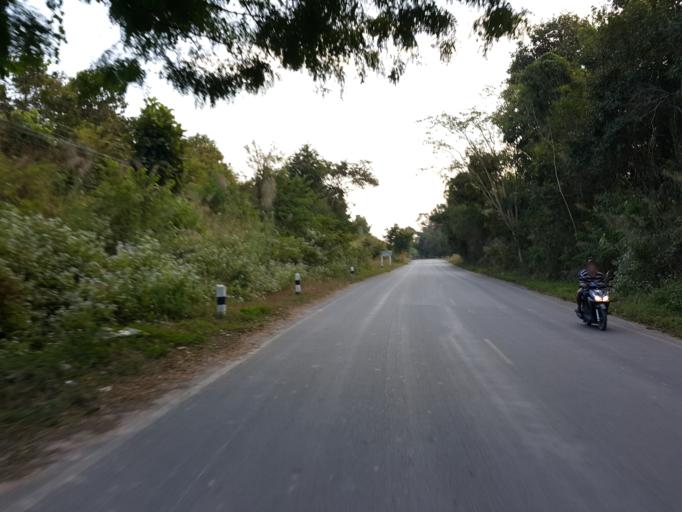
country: TH
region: Lamphun
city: Thung Hua Chang
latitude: 17.9609
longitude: 99.0455
